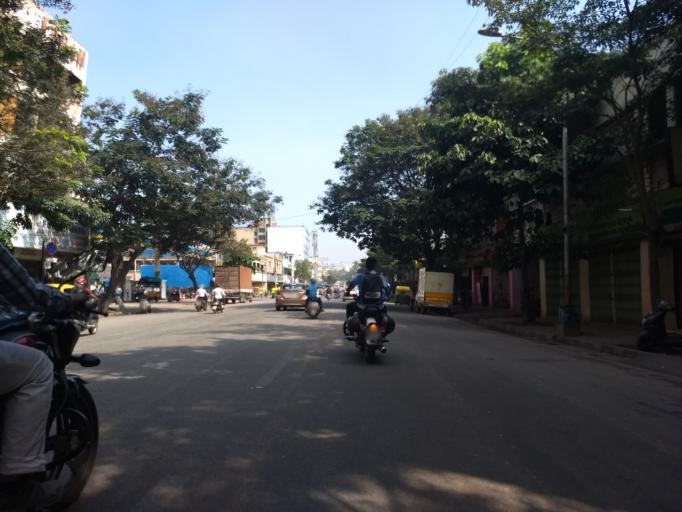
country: IN
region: Karnataka
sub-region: Bangalore Urban
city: Bangalore
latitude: 12.9583
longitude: 77.5825
